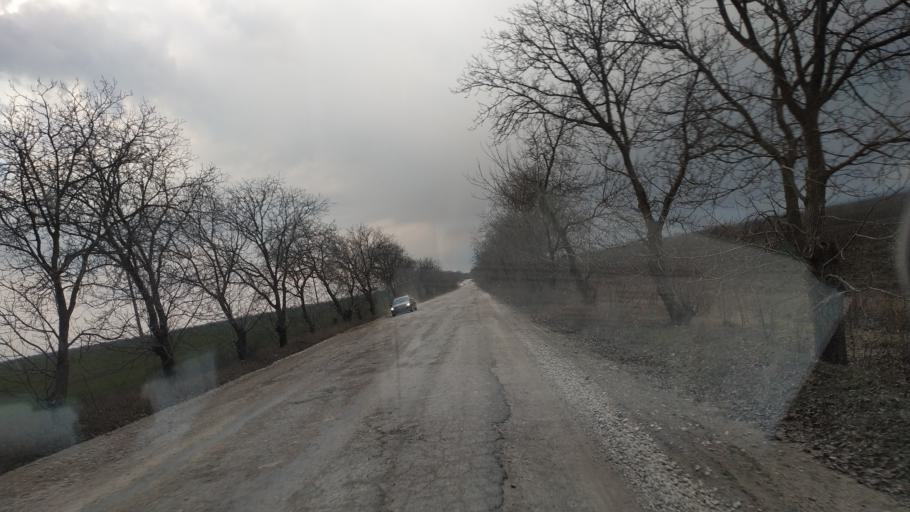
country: MD
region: Telenesti
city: Grigoriopol
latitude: 47.0351
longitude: 29.2930
